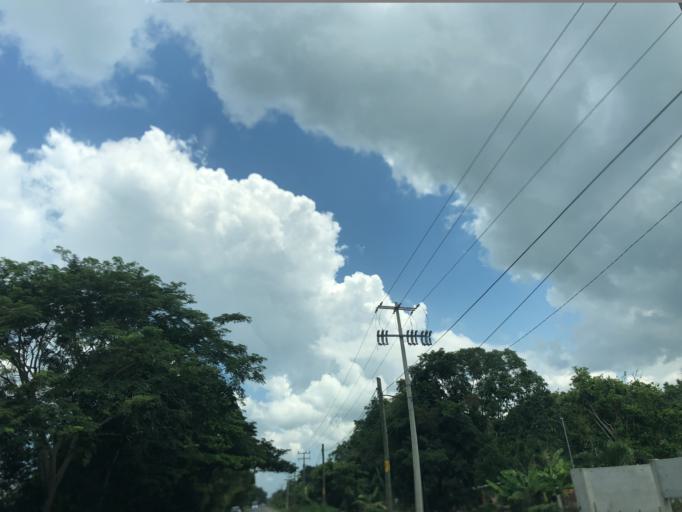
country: MX
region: Tabasco
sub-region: Comalcalco
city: Oriente 6ta. Seccion (Los Mulatos)
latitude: 18.1770
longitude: -93.2351
